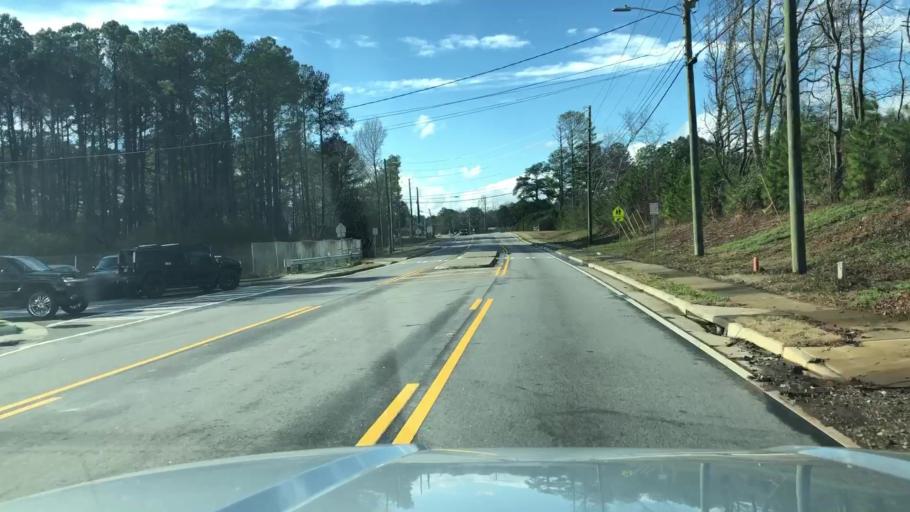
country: US
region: Georgia
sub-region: Clayton County
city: Riverdale
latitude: 33.6083
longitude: -84.4410
